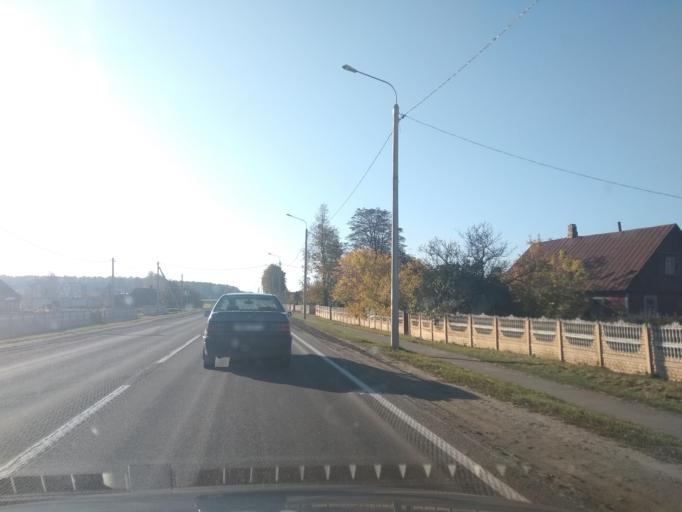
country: BY
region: Grodnenskaya
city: Vyalikaya Byerastavitsa
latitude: 53.1168
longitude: 23.9745
